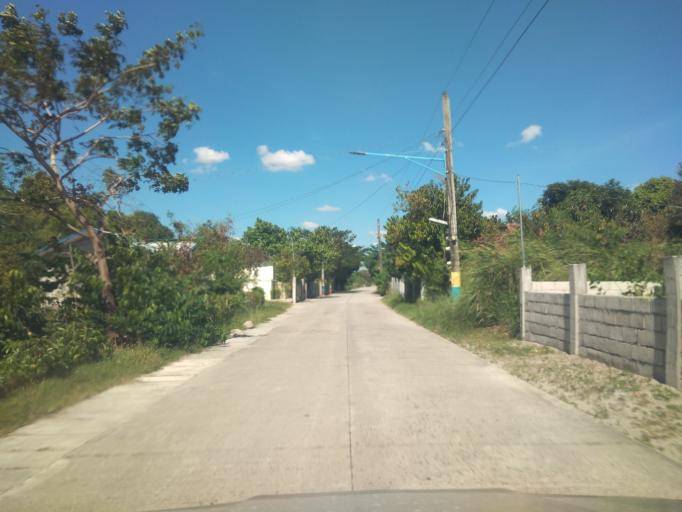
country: PH
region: Central Luzon
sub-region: Province of Pampanga
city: Santa Rita
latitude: 15.0332
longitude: 120.6233
